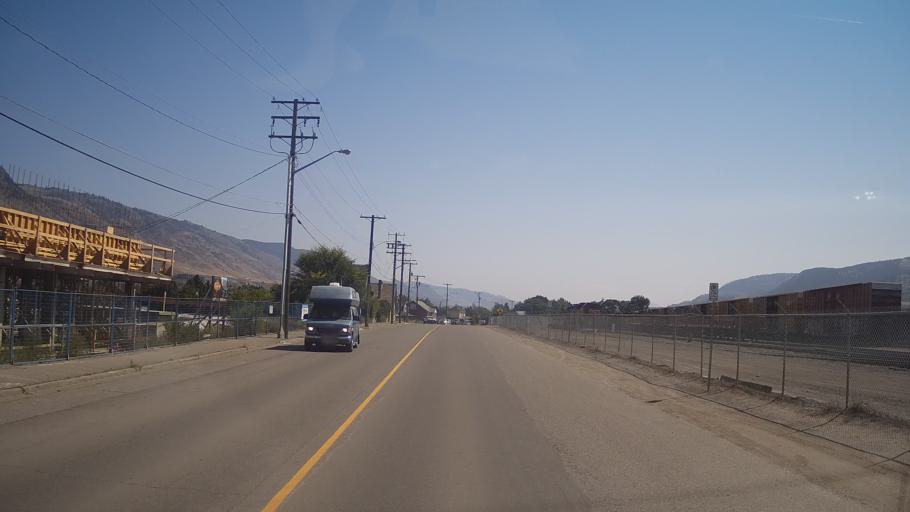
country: CA
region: British Columbia
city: Kamloops
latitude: 50.6783
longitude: -120.3278
